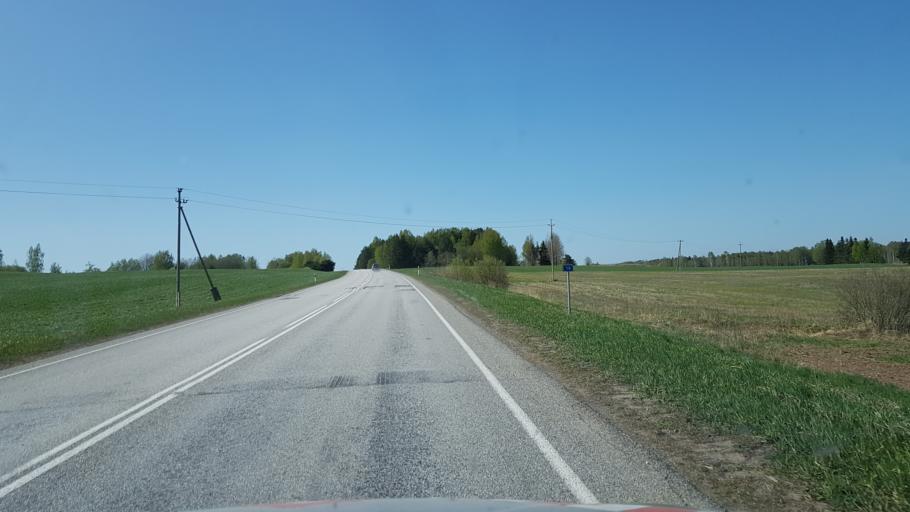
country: EE
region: Valgamaa
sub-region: Torva linn
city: Torva
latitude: 57.9160
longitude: 26.0306
